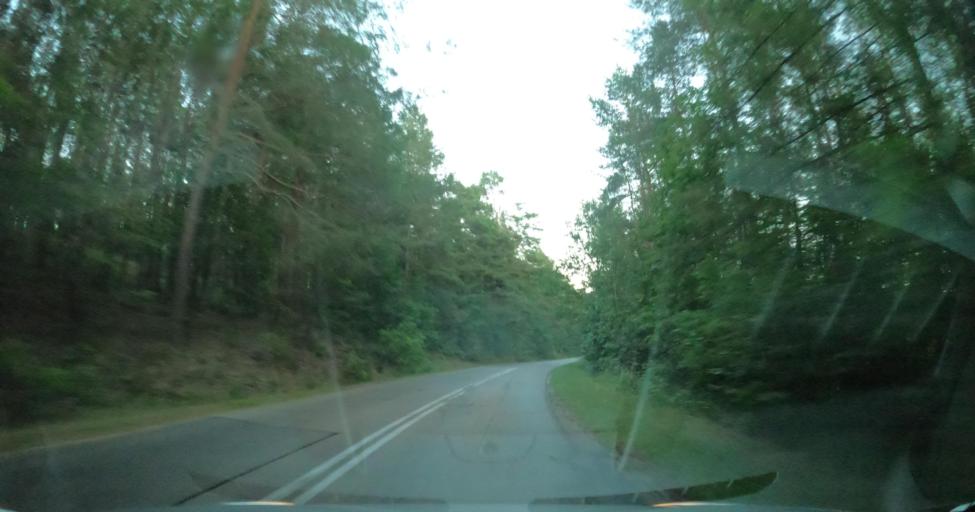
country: PL
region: Pomeranian Voivodeship
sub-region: Powiat wejherowski
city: Linia
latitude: 54.4607
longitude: 18.0002
